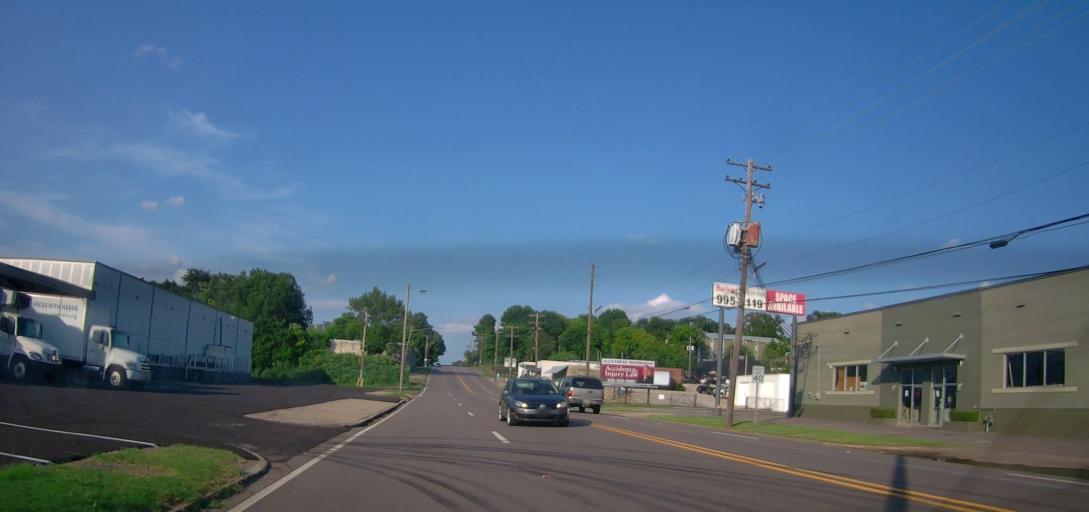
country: US
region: Alabama
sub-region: Jefferson County
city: Birmingham
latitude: 33.5209
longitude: -86.7799
